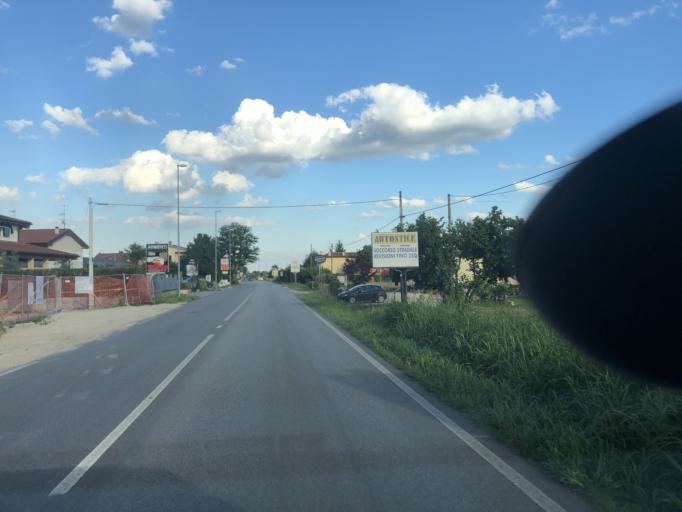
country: IT
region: Veneto
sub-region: Provincia di Verona
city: Pescantina
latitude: 45.4942
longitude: 10.8768
